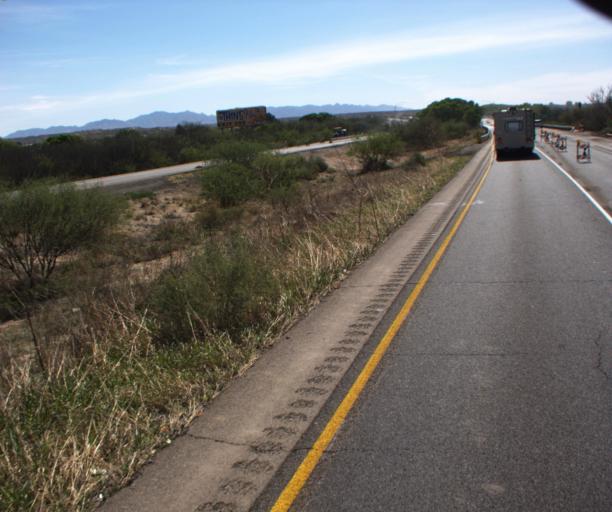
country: US
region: Arizona
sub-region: Cochise County
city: Benson
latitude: 31.9697
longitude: -110.2815
